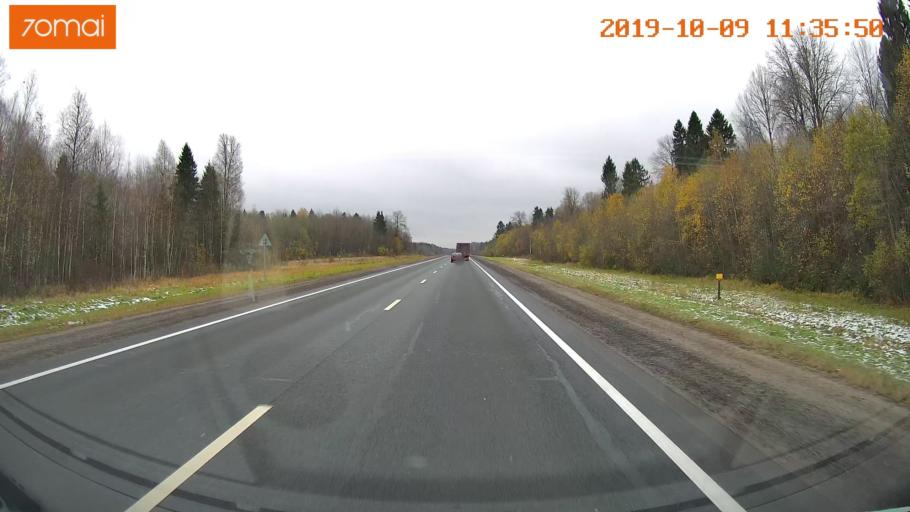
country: RU
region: Vologda
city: Gryazovets
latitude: 58.9983
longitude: 40.1303
